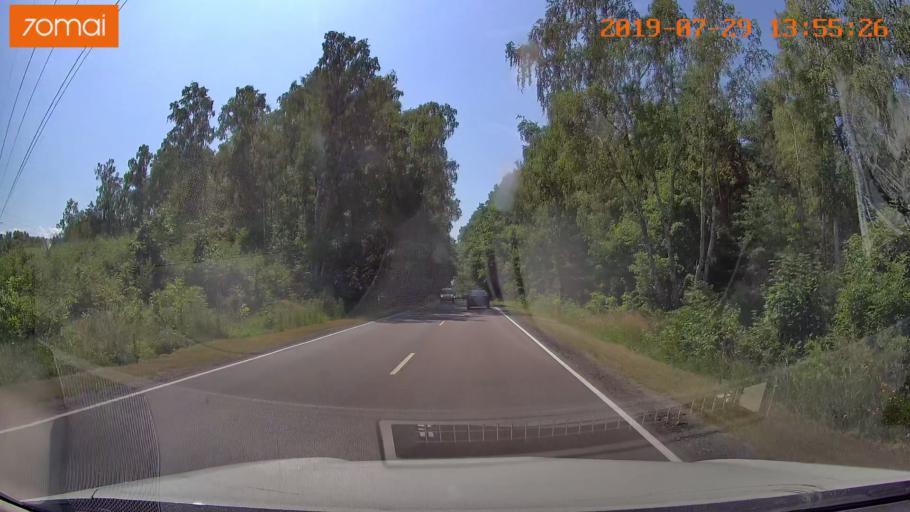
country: RU
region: Kaliningrad
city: Primorsk
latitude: 54.7153
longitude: 19.9570
